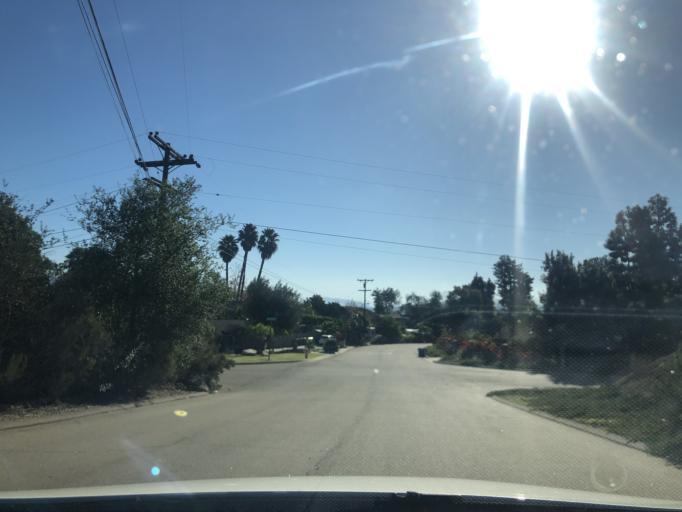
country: US
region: California
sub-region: San Diego County
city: Casa de Oro-Mount Helix
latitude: 32.7651
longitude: -116.9475
